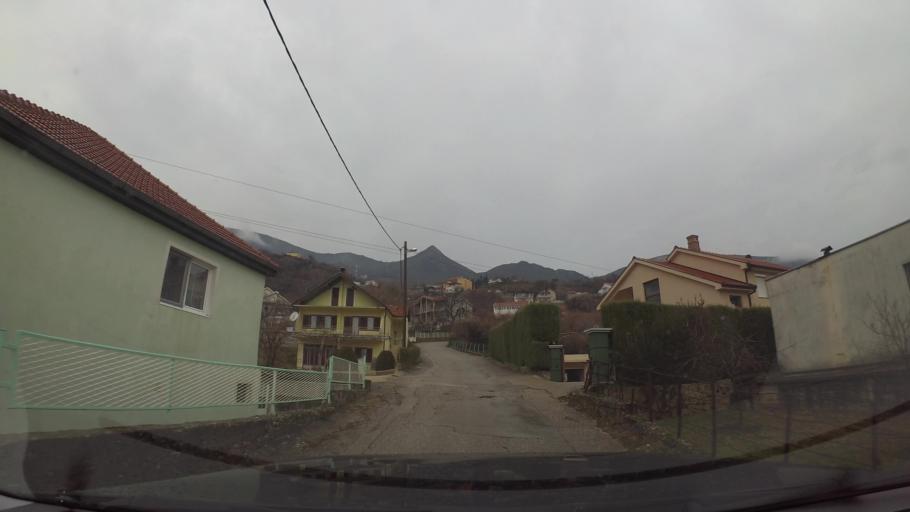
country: BA
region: Federation of Bosnia and Herzegovina
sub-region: Hercegovacko-Bosanski Kanton
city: Mostar
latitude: 43.3619
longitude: 17.8030
